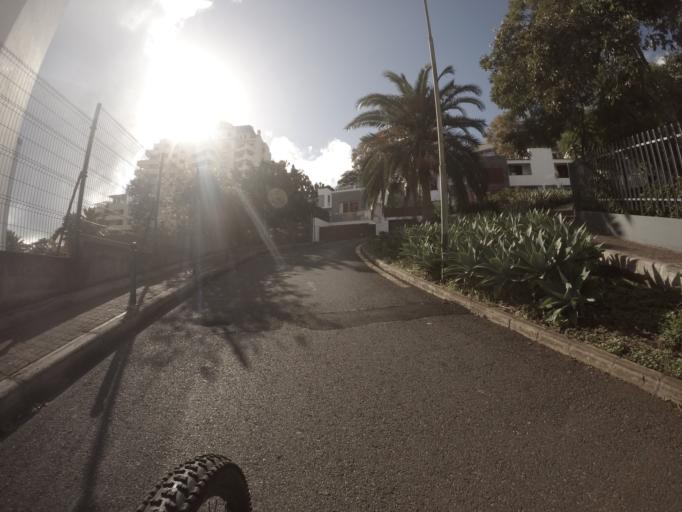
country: PT
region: Madeira
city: Camara de Lobos
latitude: 32.6358
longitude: -16.9399
